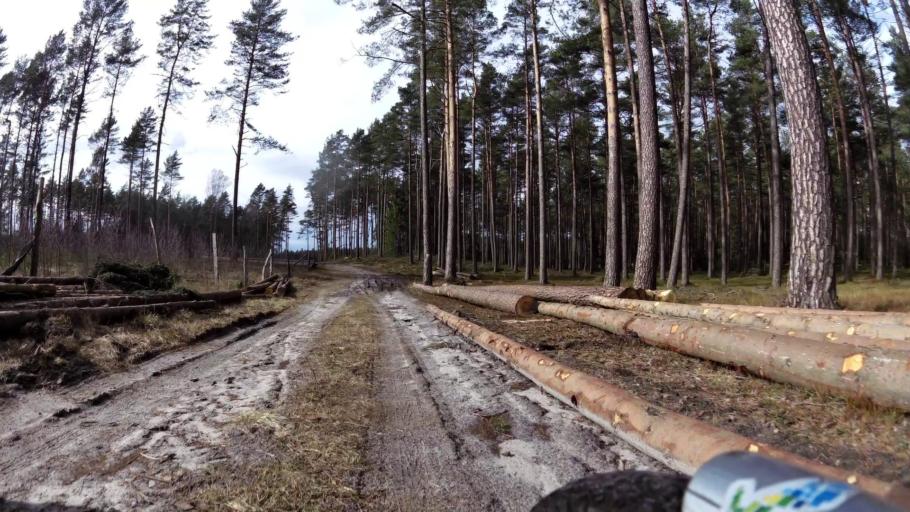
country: PL
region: Pomeranian Voivodeship
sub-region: Powiat bytowski
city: Kolczyglowy
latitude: 54.1507
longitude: 17.1790
